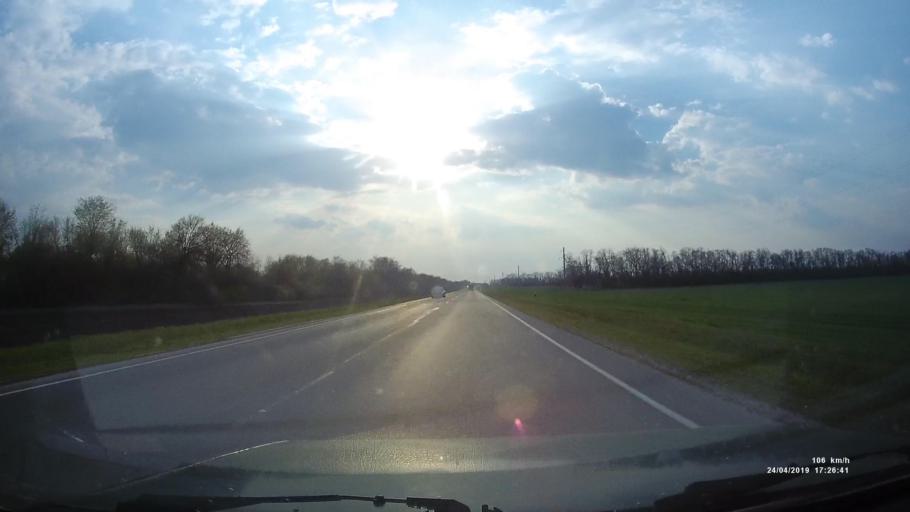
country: RU
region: Rostov
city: Gigant
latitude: 46.5273
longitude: 41.2141
